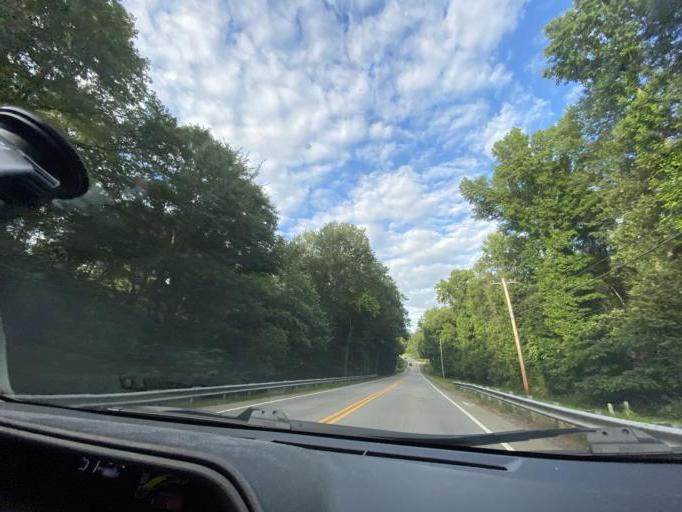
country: US
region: Georgia
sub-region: Fulton County
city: Palmetto
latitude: 33.4459
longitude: -84.6703
